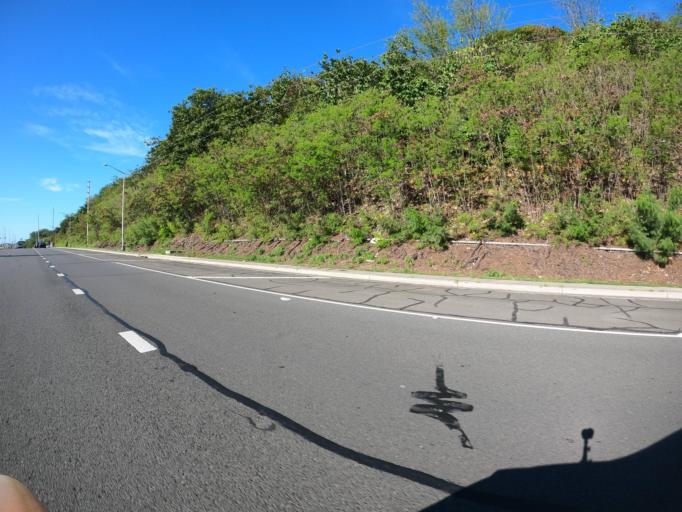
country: US
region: Hawaii
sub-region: Honolulu County
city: Halawa Heights
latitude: 21.3467
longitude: -157.8982
